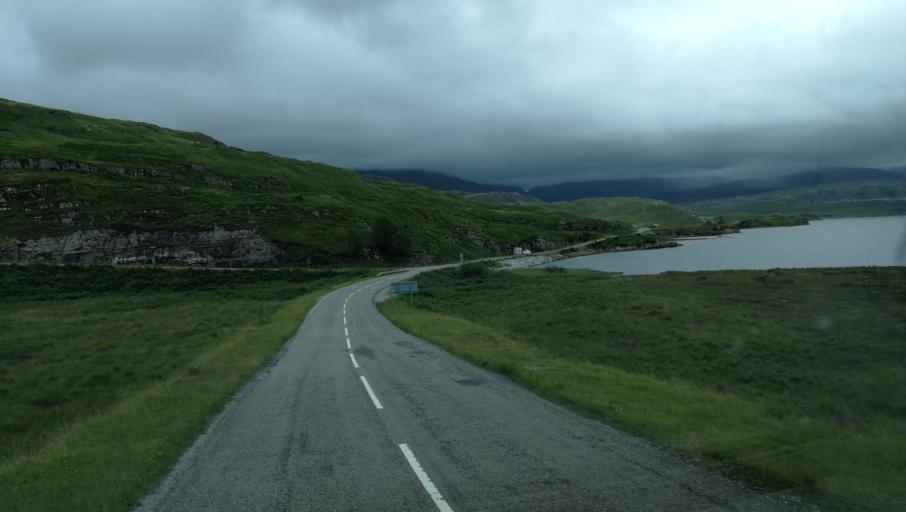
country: GB
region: Scotland
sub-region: Highland
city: Ullapool
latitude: 58.1736
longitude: -5.0054
